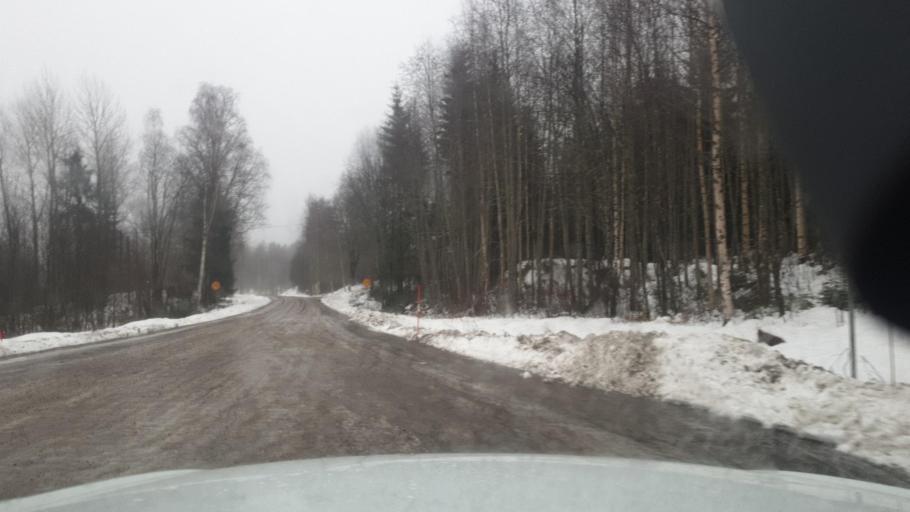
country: SE
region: Vaermland
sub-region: Eda Kommun
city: Charlottenberg
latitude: 60.0928
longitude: 12.4956
